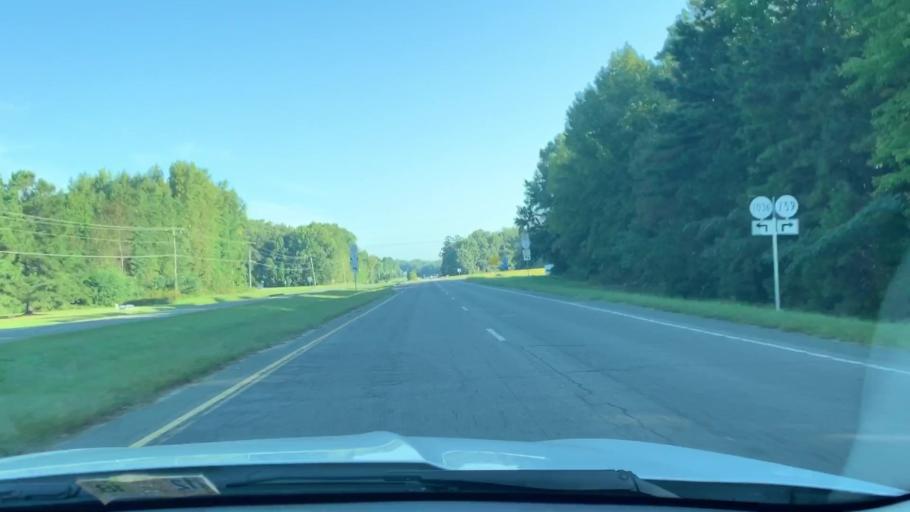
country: US
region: Virginia
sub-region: Lancaster County
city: Kilmarnock
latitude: 37.6862
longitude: -76.3768
